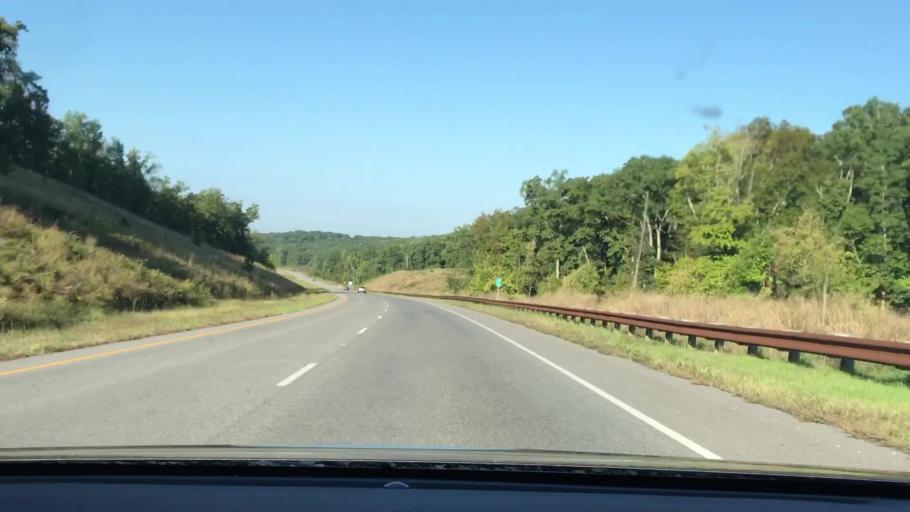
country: US
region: Kentucky
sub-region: Trigg County
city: Cadiz
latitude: 36.7797
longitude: -88.0864
